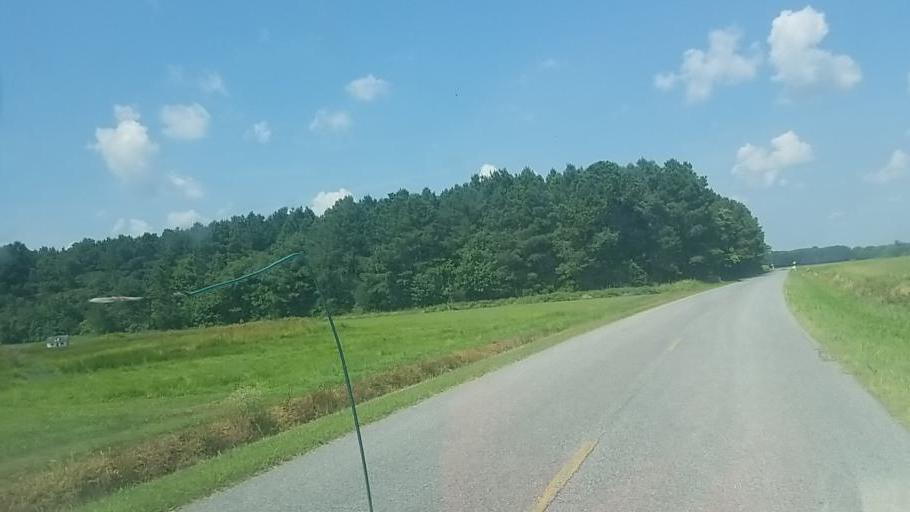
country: US
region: Maryland
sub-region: Worcester County
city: Berlin
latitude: 38.2969
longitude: -75.2663
